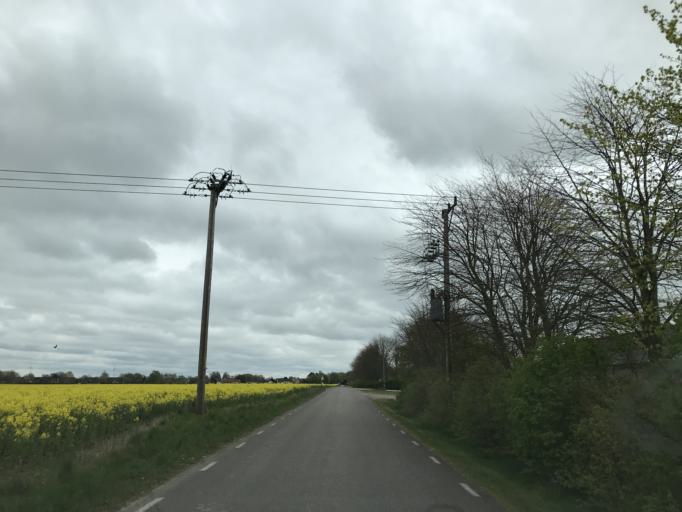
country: SE
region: Skane
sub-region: Svalovs Kommun
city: Teckomatorp
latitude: 55.8646
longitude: 13.0737
